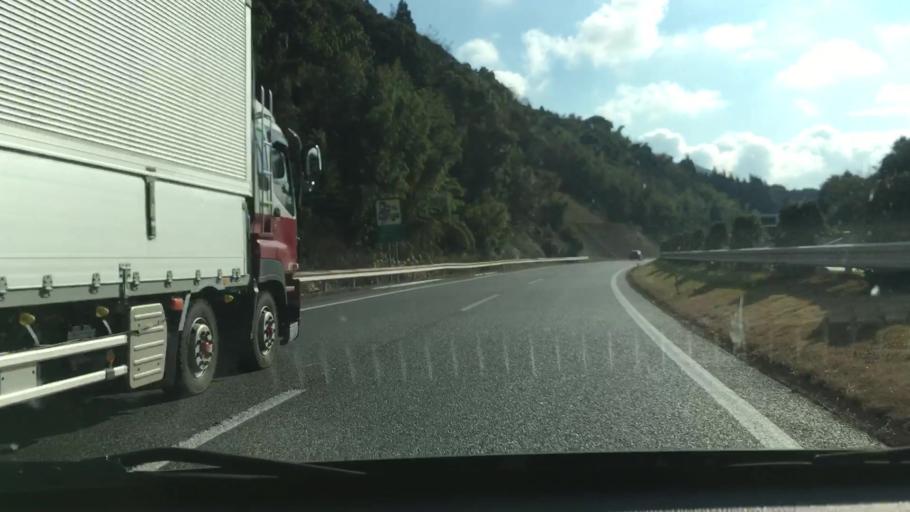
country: JP
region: Kumamoto
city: Matsubase
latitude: 32.6111
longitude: 130.7247
